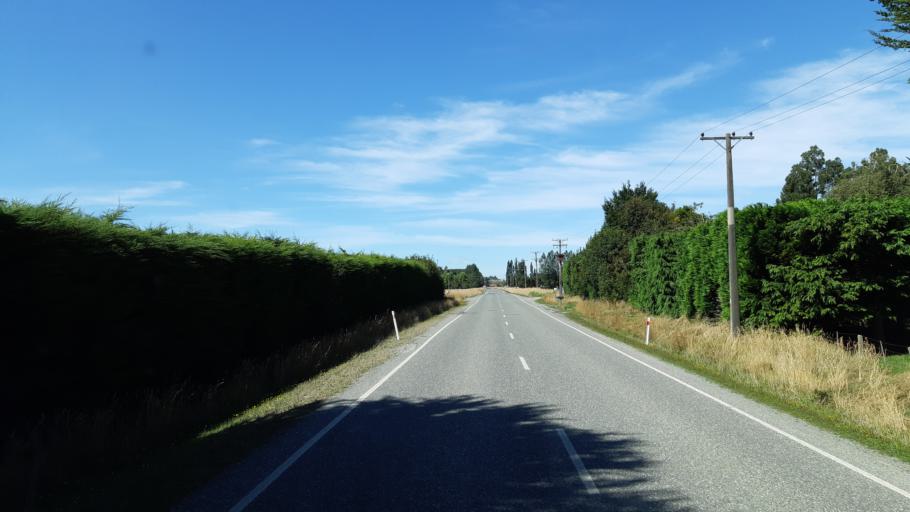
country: NZ
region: Southland
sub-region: Gore District
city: Gore
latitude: -46.0007
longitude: 168.8680
